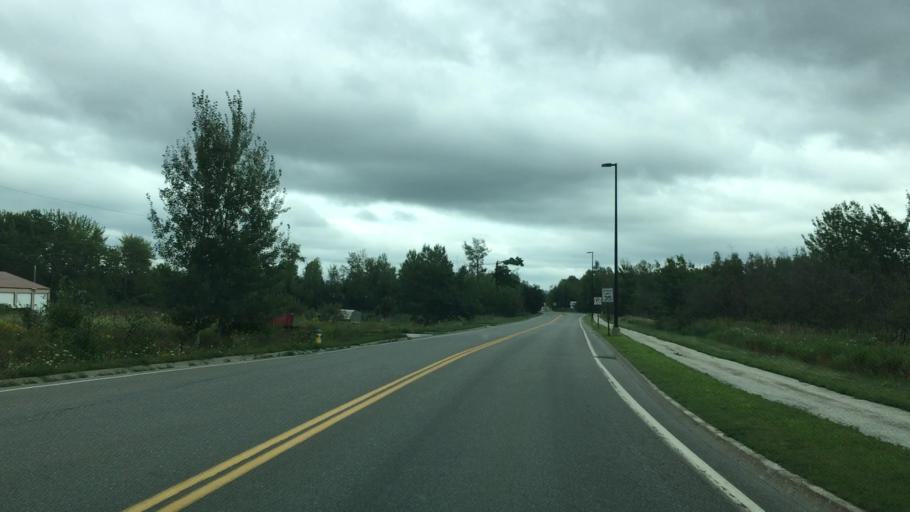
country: US
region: Maine
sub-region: Penobscot County
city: Brewer
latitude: 44.7769
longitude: -68.7435
